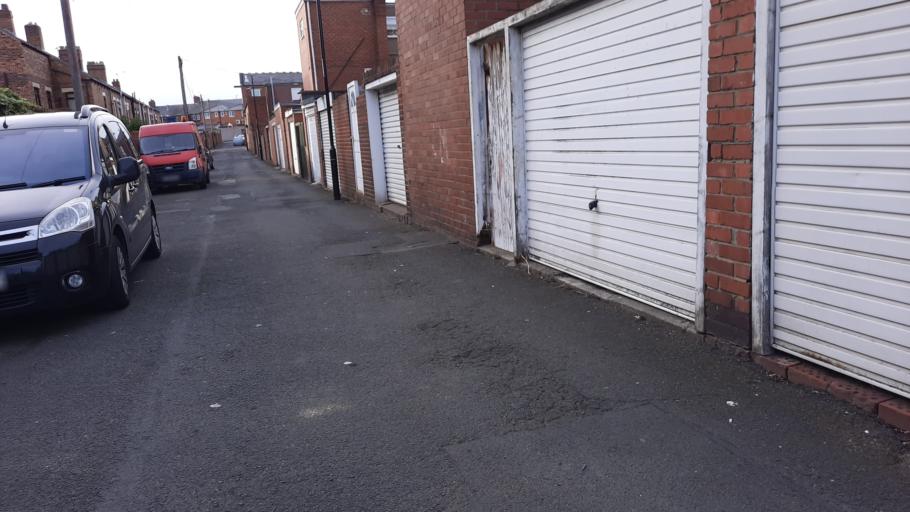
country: GB
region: England
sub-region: County Durham
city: Houghton-le-Spring
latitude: 54.8671
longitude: -1.4929
